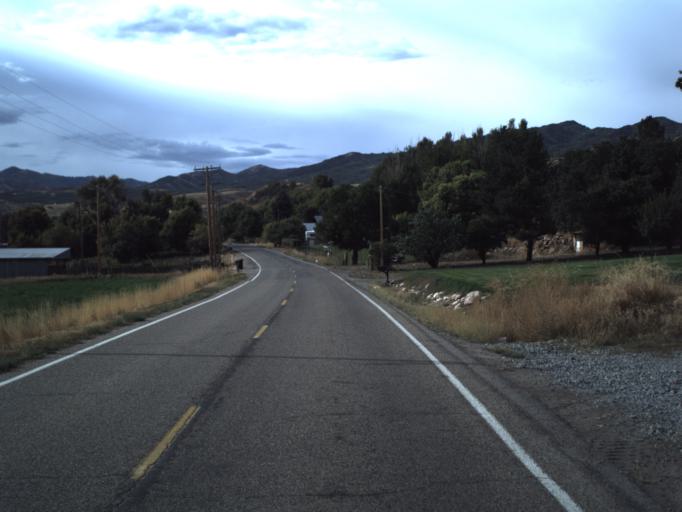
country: US
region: Utah
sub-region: Morgan County
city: Morgan
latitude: 40.9728
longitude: -111.6729
